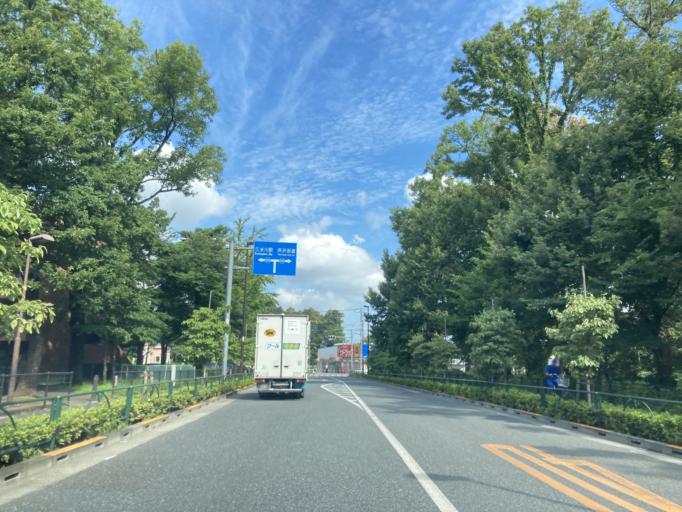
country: JP
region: Tokyo
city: Higashimurayama-shi
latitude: 35.7609
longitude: 139.4918
